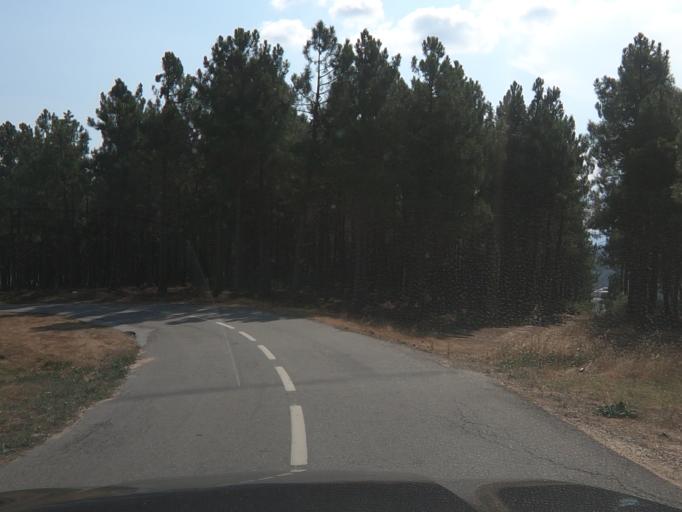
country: PT
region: Vila Real
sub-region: Sabrosa
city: Sabrosa
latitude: 41.2755
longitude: -7.6199
